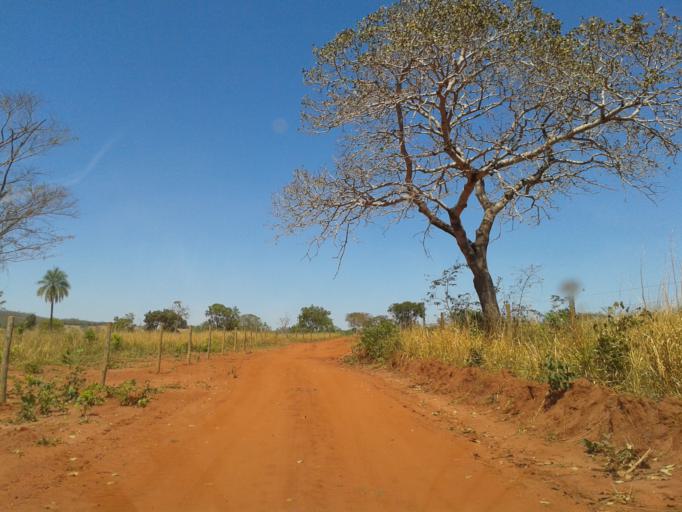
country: BR
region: Minas Gerais
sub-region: Ituiutaba
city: Ituiutaba
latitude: -19.0877
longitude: -49.2644
